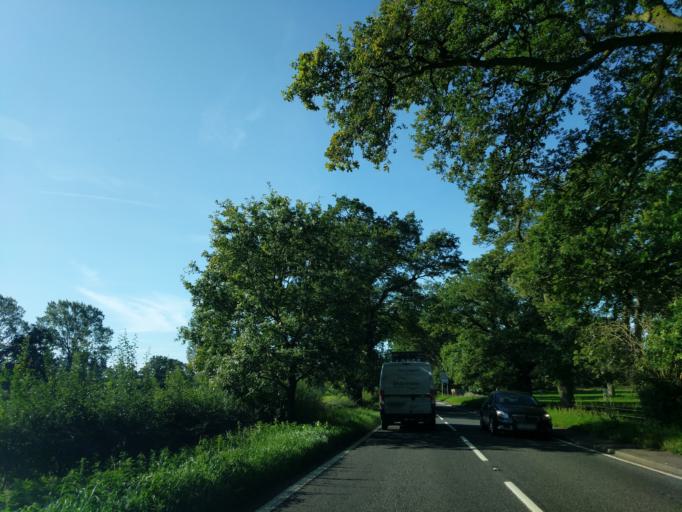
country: GB
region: England
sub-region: Lincolnshire
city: Bourne
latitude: 52.7928
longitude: -0.4448
